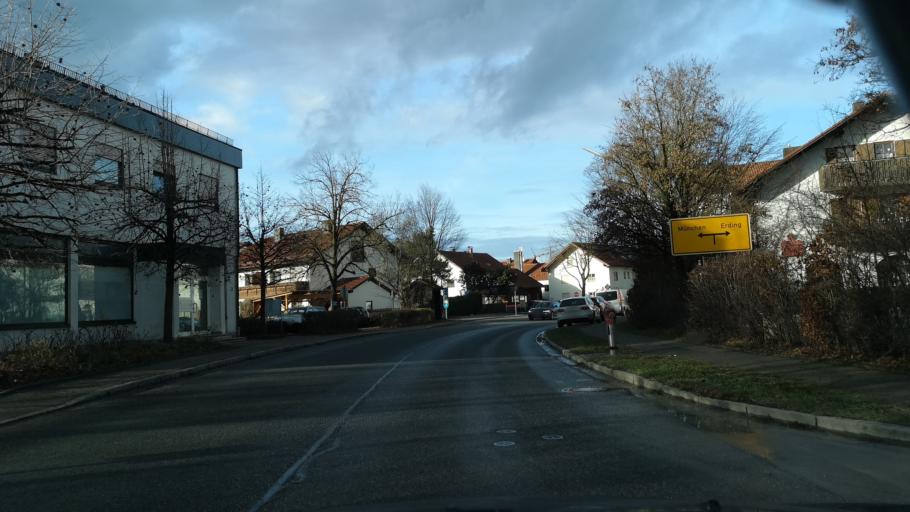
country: DE
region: Bavaria
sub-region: Upper Bavaria
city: Pliening
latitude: 48.1963
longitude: 11.7991
